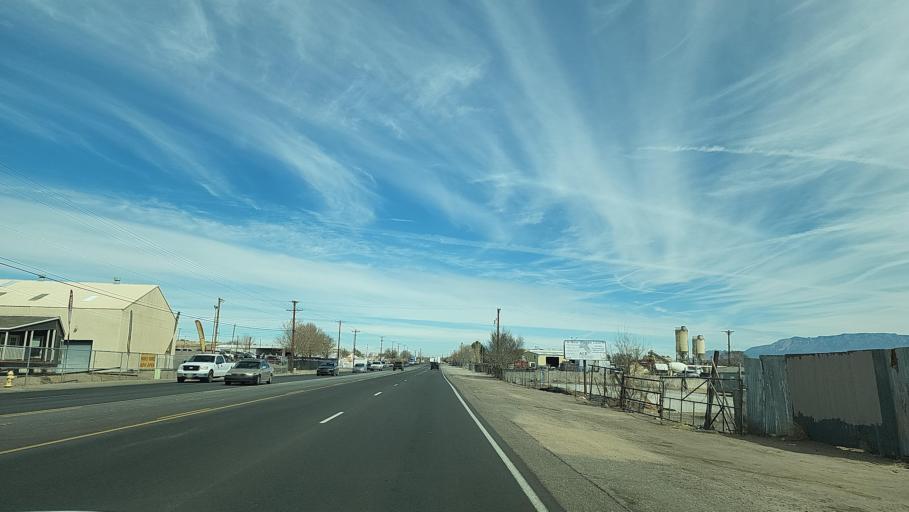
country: US
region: New Mexico
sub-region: Bernalillo County
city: South Valley
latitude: 35.0446
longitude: -106.7098
